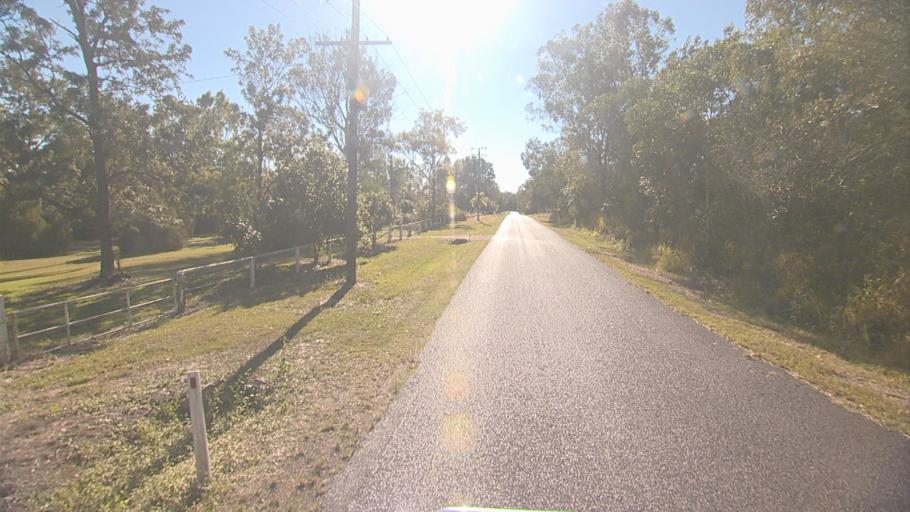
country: AU
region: Queensland
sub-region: Logan
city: Chambers Flat
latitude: -27.7470
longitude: 153.0846
